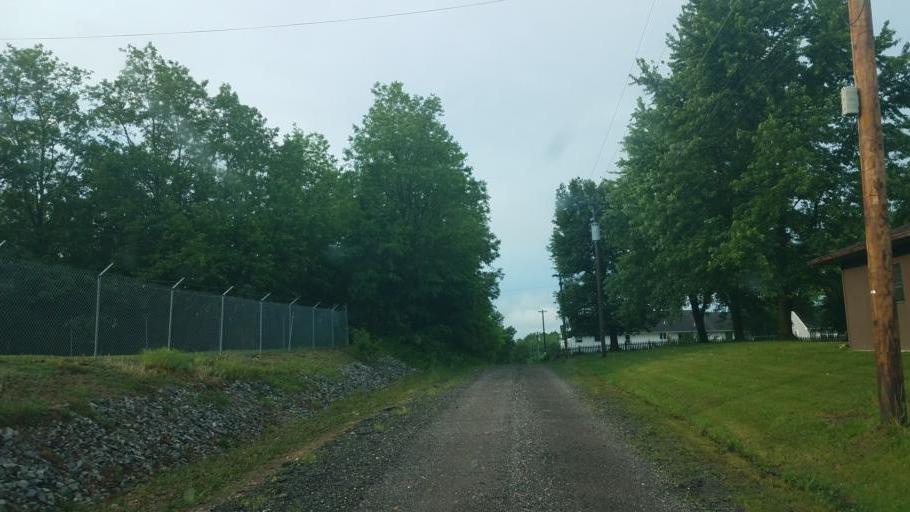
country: US
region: Missouri
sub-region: Moniteau County
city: California
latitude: 38.6227
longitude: -92.5586
